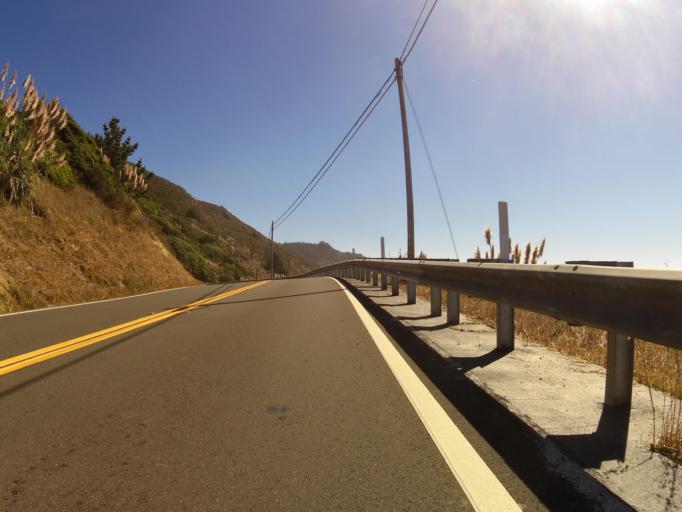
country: US
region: California
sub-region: Mendocino County
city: Fort Bragg
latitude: 39.6230
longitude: -123.7818
